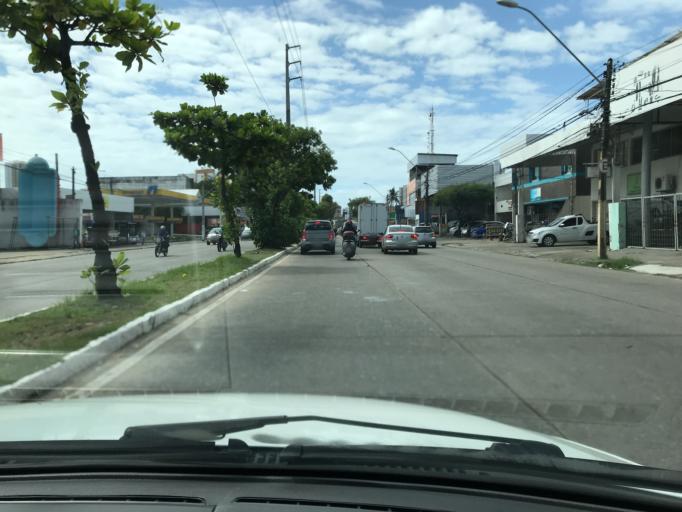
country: BR
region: Pernambuco
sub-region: Recife
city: Recife
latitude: -8.0621
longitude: -34.9092
